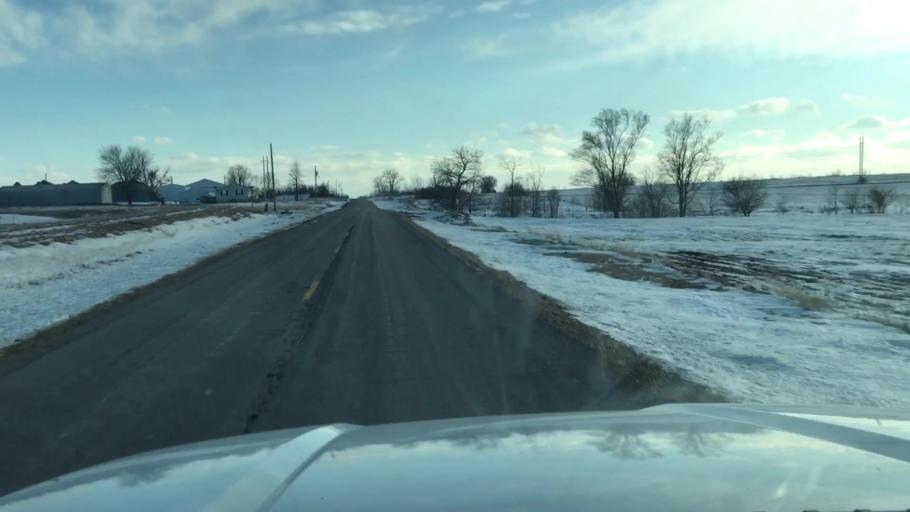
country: US
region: Missouri
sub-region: Holt County
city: Oregon
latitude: 40.1163
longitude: -95.0226
